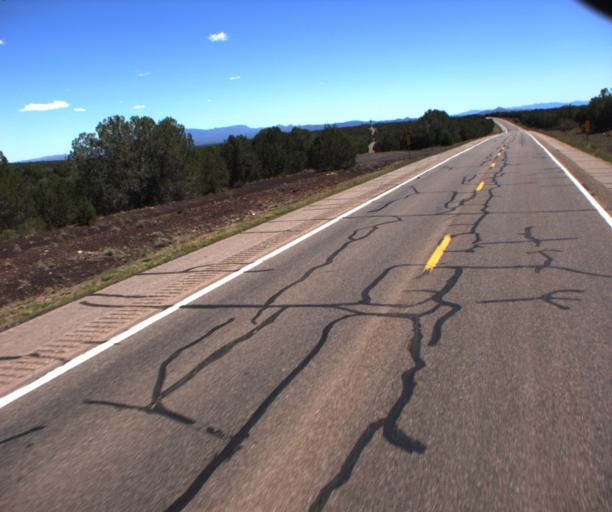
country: US
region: Arizona
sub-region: Yavapai County
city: Paulden
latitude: 35.0436
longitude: -112.3959
